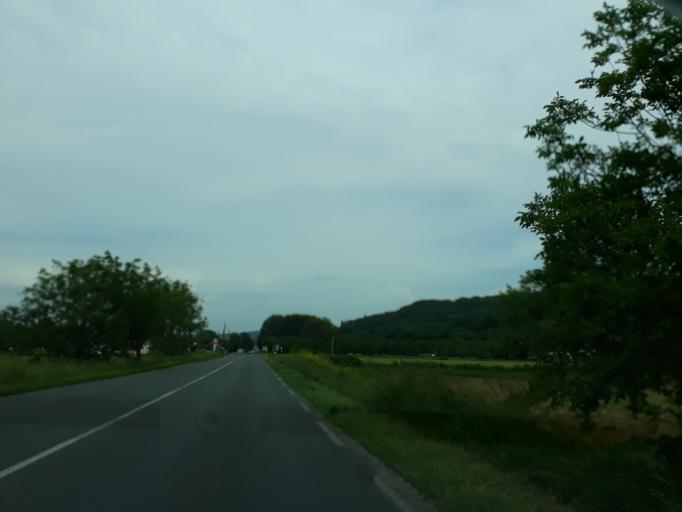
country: FR
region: Limousin
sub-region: Departement de la Correze
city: Cublac
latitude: 45.1278
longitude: 1.3378
